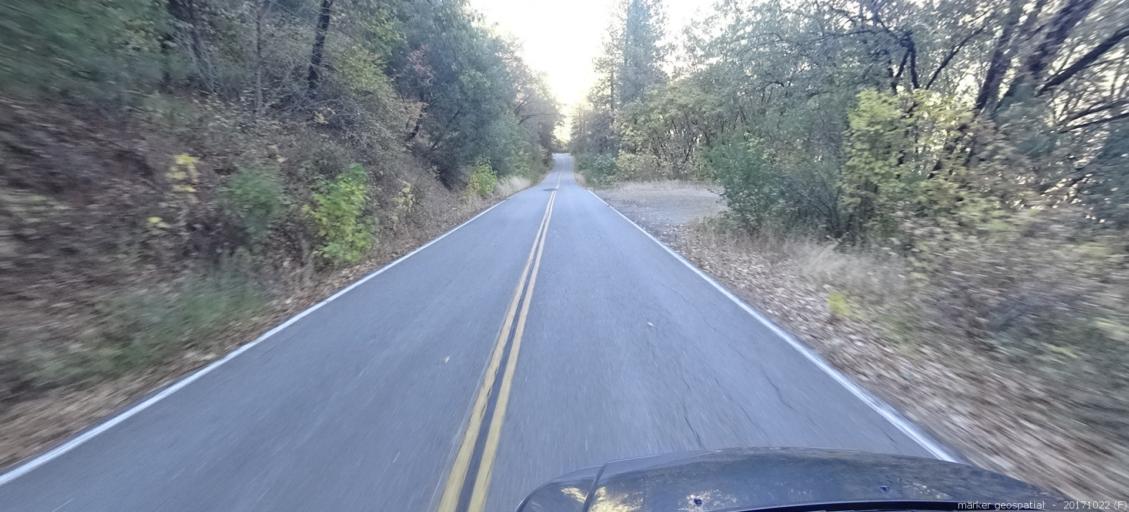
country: US
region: California
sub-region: Shasta County
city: Shasta Lake
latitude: 40.9074
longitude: -122.2366
